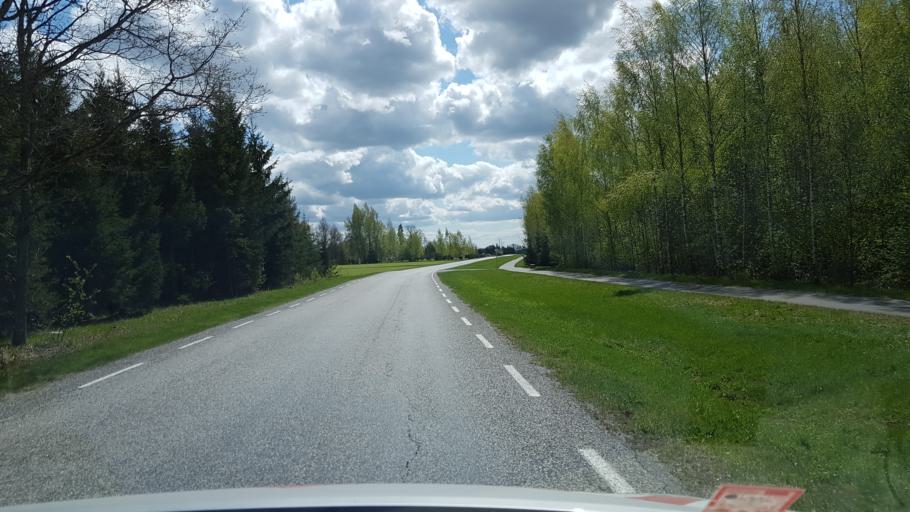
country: EE
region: Jogevamaa
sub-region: Poltsamaa linn
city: Poltsamaa
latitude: 58.6908
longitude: 25.9468
